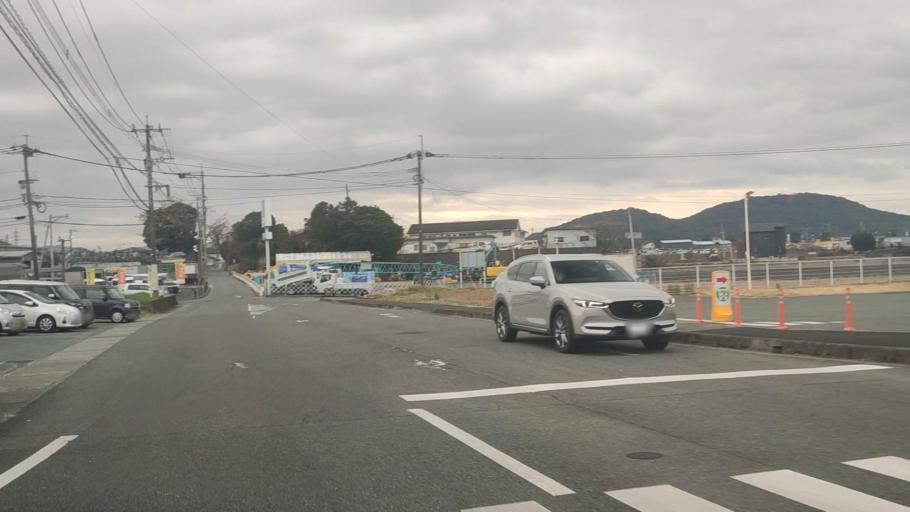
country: JP
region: Kumamoto
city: Ozu
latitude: 32.8306
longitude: 130.7981
